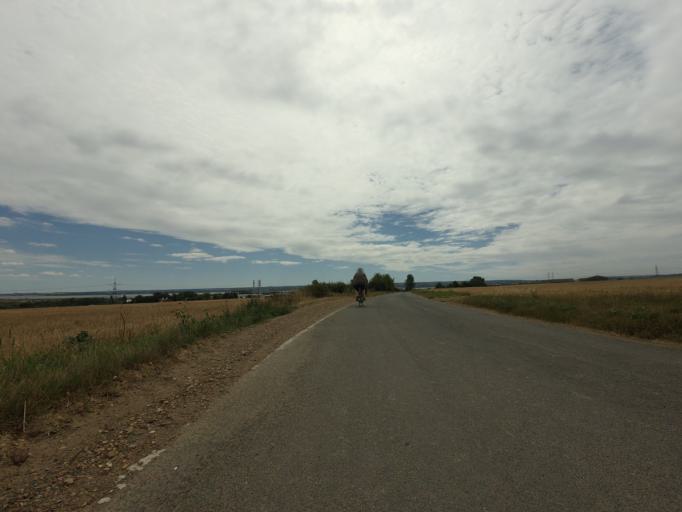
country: GB
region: England
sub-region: Medway
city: Stoke
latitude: 51.4388
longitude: 0.5986
